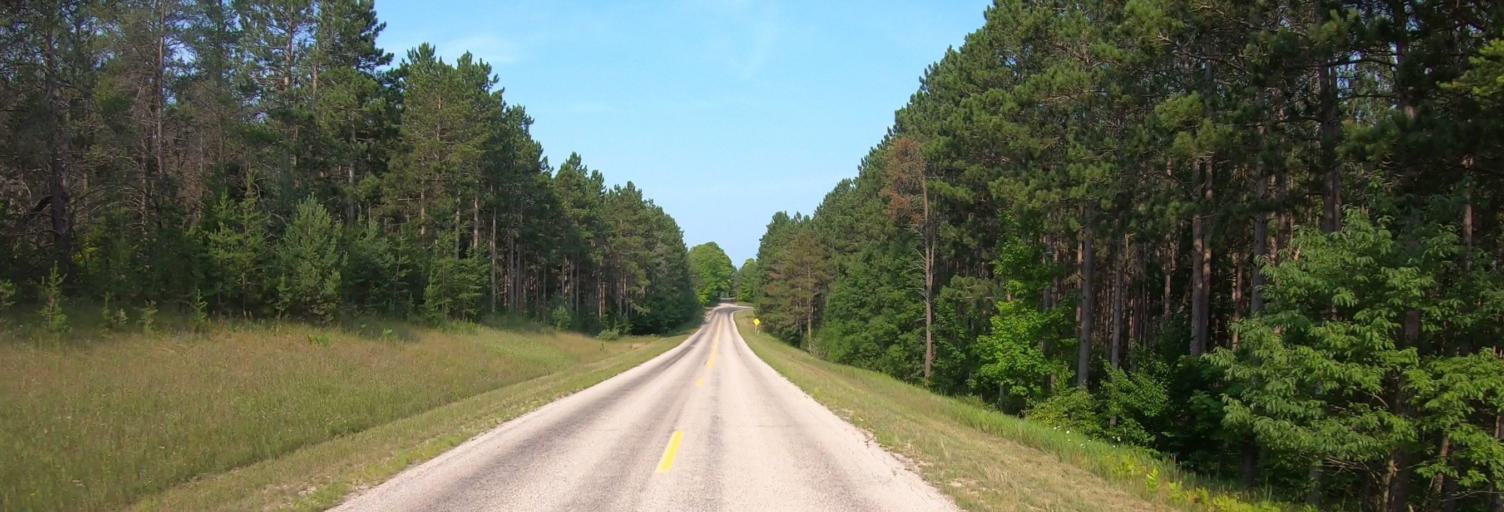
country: US
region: Michigan
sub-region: Benzie County
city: Beulah
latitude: 44.7785
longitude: -85.9540
